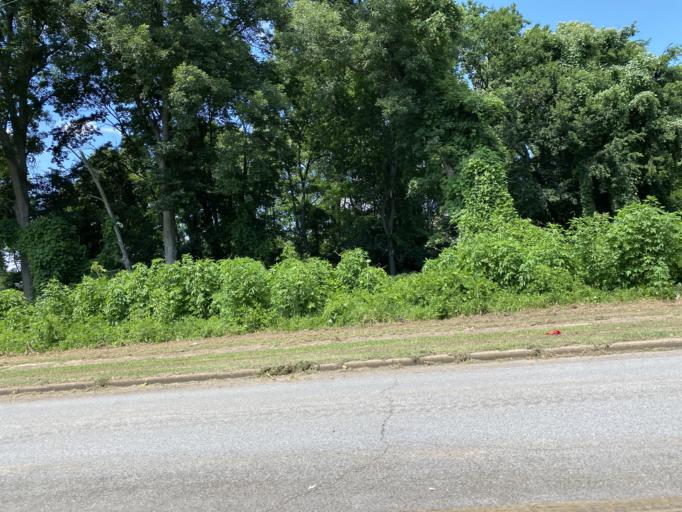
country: US
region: Alabama
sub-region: Morgan County
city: Decatur
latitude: 34.6121
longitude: -86.9900
